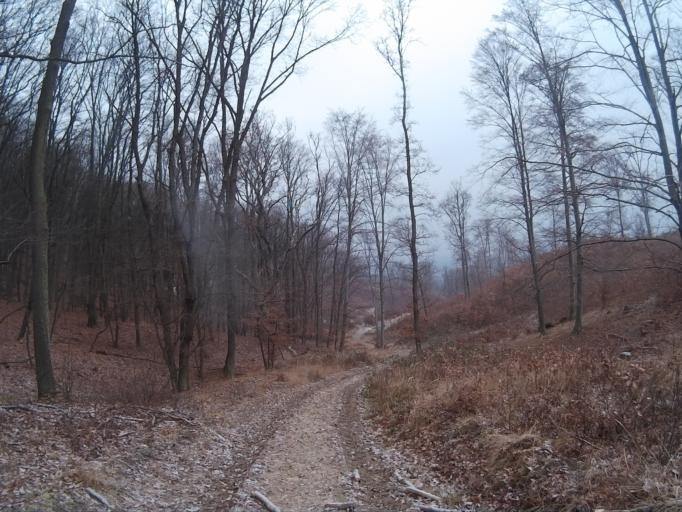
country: HU
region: Nograd
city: Rimoc
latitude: 47.9825
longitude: 19.5694
